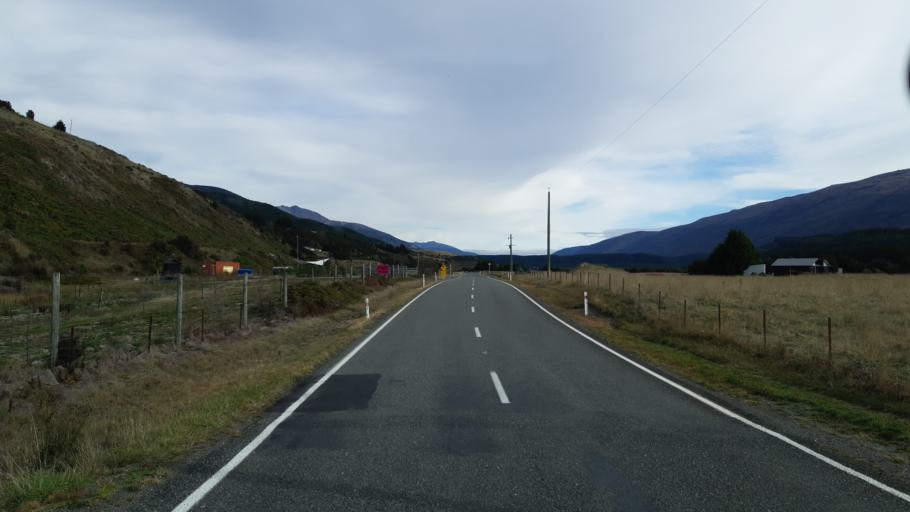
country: NZ
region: Tasman
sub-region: Tasman District
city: Brightwater
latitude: -41.6868
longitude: 173.1578
